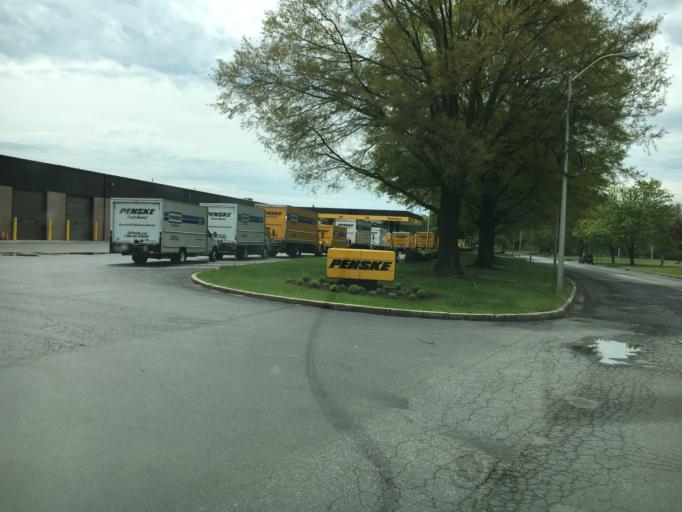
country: US
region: Pennsylvania
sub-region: Berks County
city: West Reading
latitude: 40.3325
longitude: -75.9373
